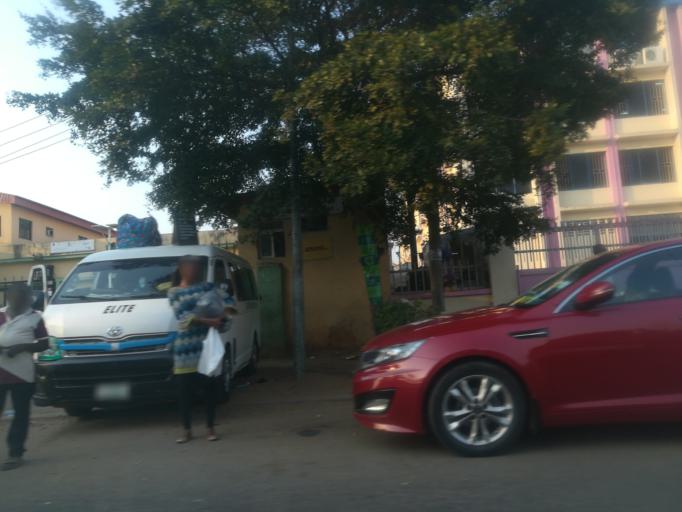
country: NG
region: Abuja Federal Capital Territory
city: Abuja
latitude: 9.0669
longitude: 7.4429
